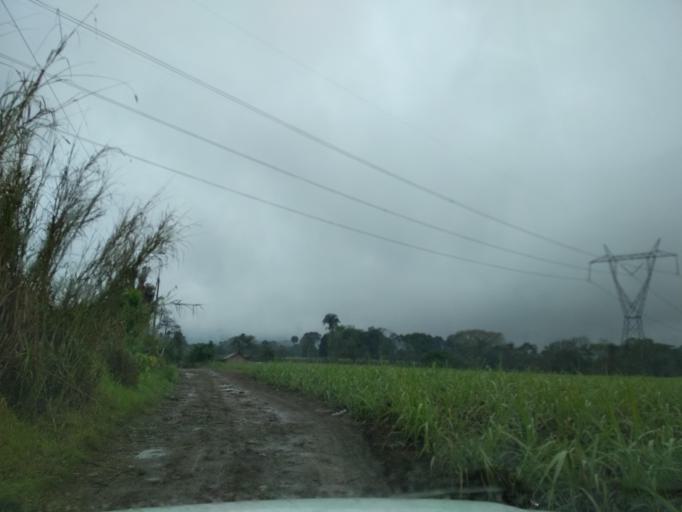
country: MX
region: Veracruz
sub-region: Amatlan de los Reyes
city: Centro de Readaptacion Social
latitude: 18.8360
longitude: -96.9287
